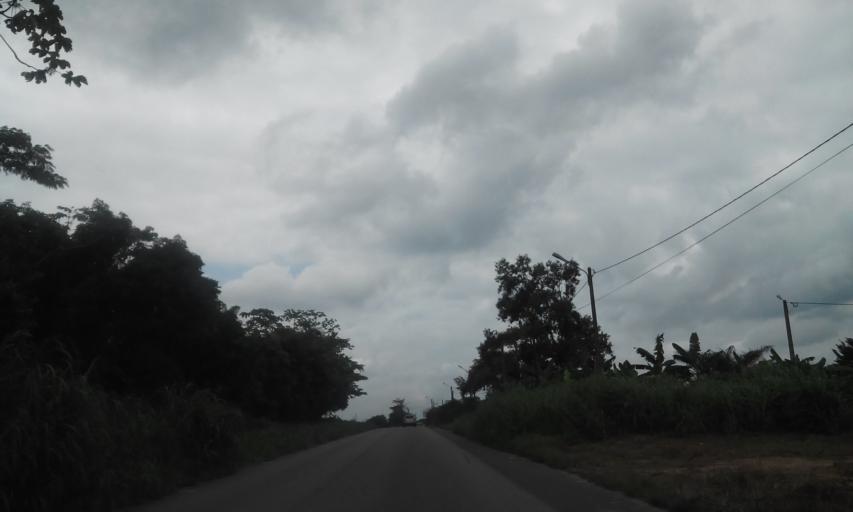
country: CI
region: Sud-Comoe
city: Aboisso
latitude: 5.4266
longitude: -3.2665
